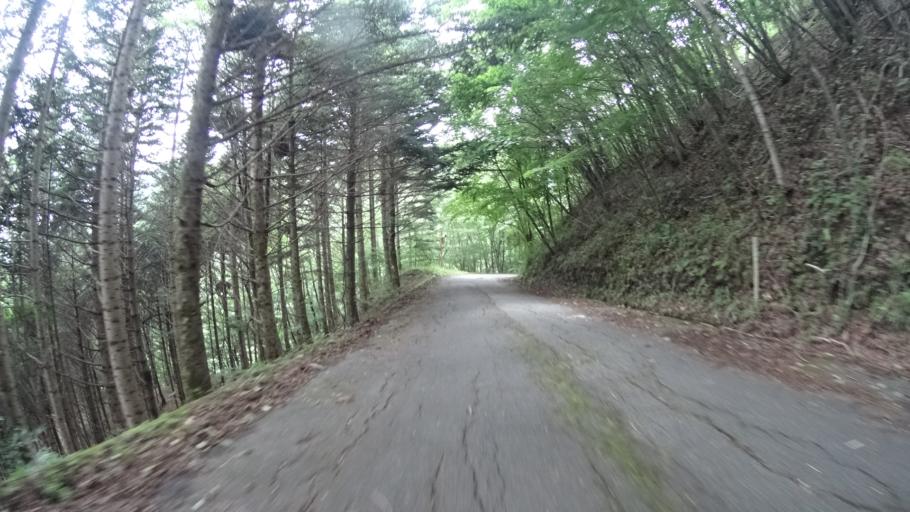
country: JP
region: Yamanashi
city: Kofu-shi
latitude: 35.8272
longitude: 138.5860
